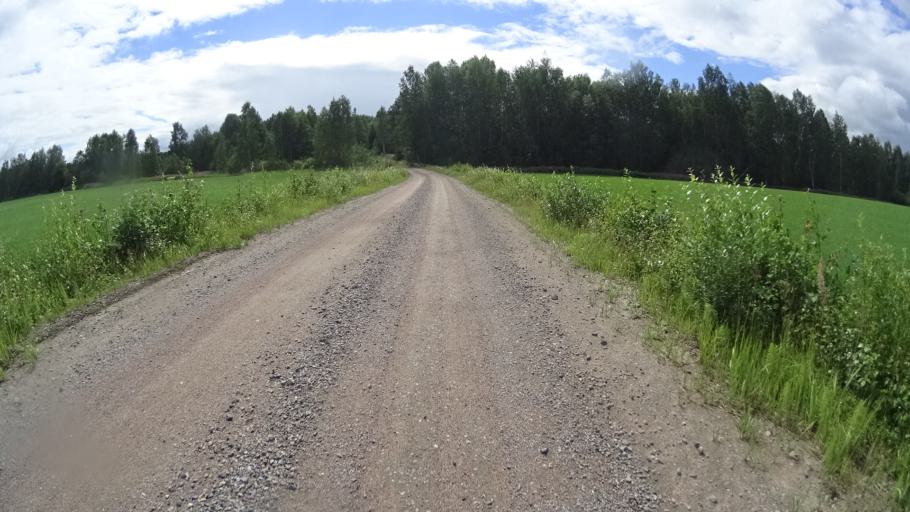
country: FI
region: Uusimaa
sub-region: Helsinki
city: Karkkila
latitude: 60.5824
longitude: 24.3000
